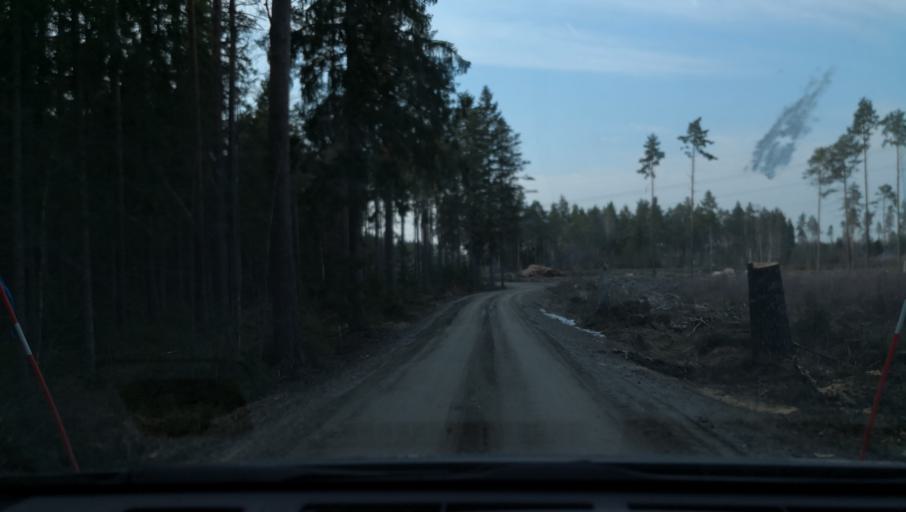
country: SE
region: OErebro
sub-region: Lindesbergs Kommun
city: Frovi
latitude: 59.3669
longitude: 15.3258
